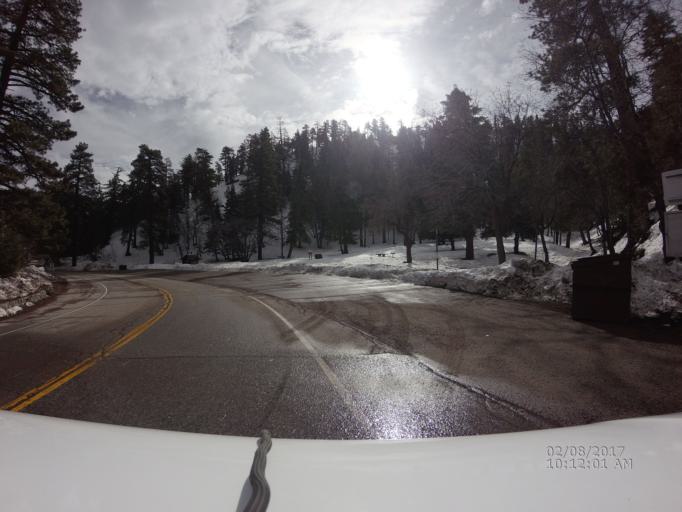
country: US
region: California
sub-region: San Bernardino County
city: Pinon Hills
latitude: 34.3870
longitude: -117.7139
